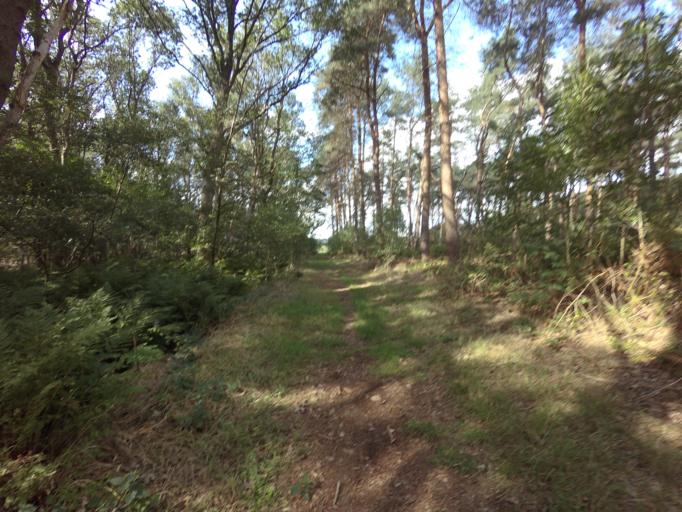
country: NL
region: Friesland
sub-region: Gemeente Heerenveen
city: Jubbega
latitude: 52.9619
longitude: 6.1997
